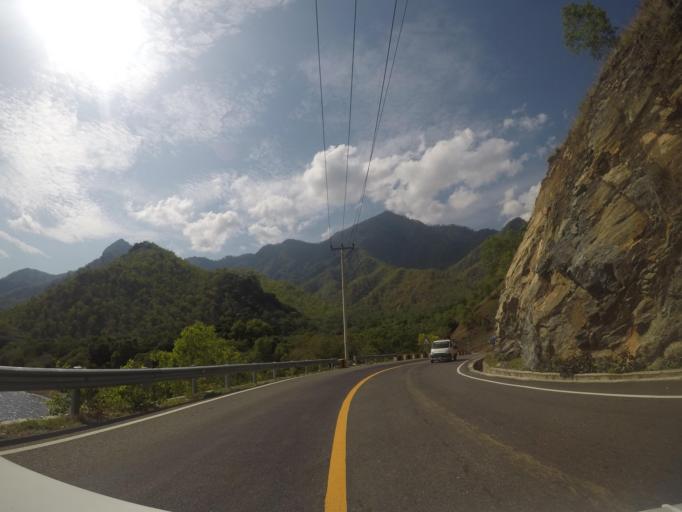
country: TL
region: Manatuto
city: Manatuto
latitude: -8.4777
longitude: 125.9073
